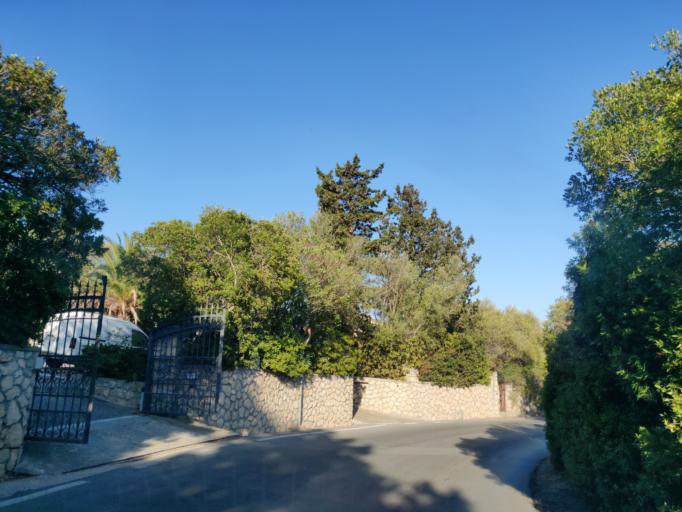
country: IT
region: Tuscany
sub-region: Provincia di Grosseto
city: Orbetello Scalo
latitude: 42.4122
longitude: 11.2935
